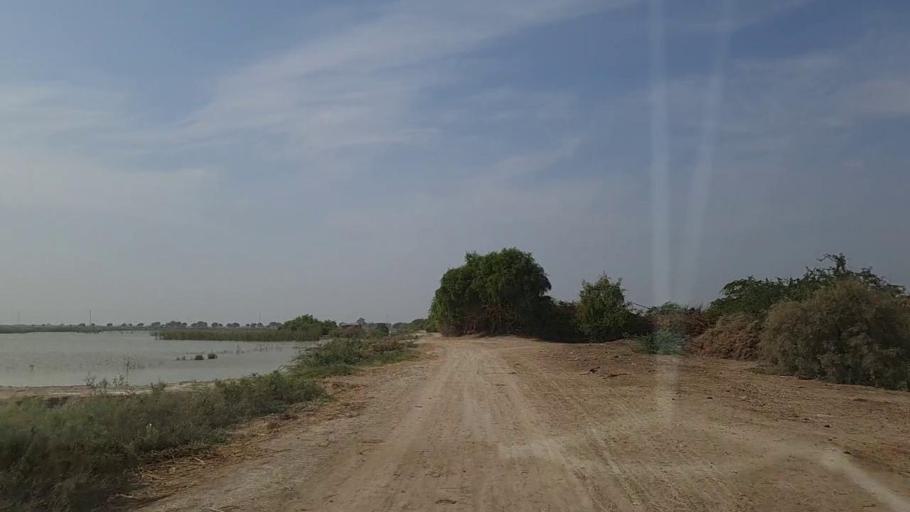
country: PK
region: Sindh
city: Mirpur Batoro
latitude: 24.6090
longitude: 68.2141
